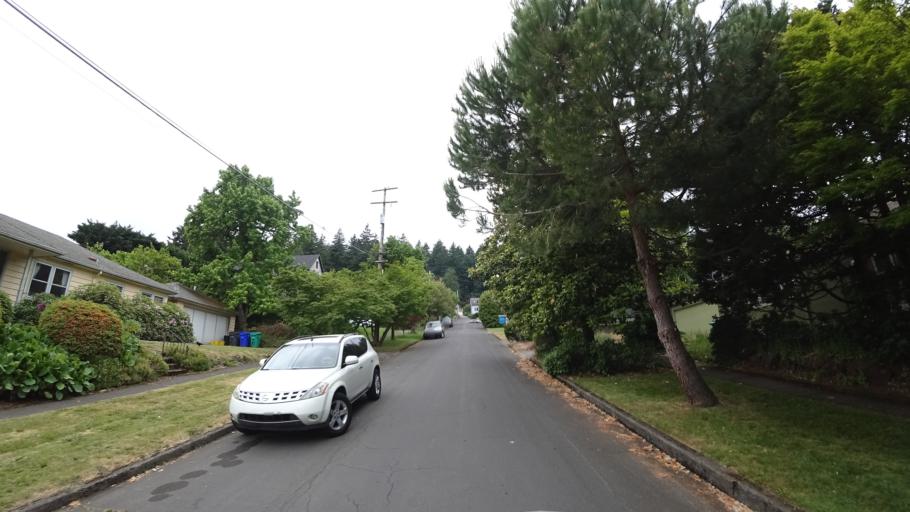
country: US
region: Oregon
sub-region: Multnomah County
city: Lents
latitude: 45.5136
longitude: -122.5878
